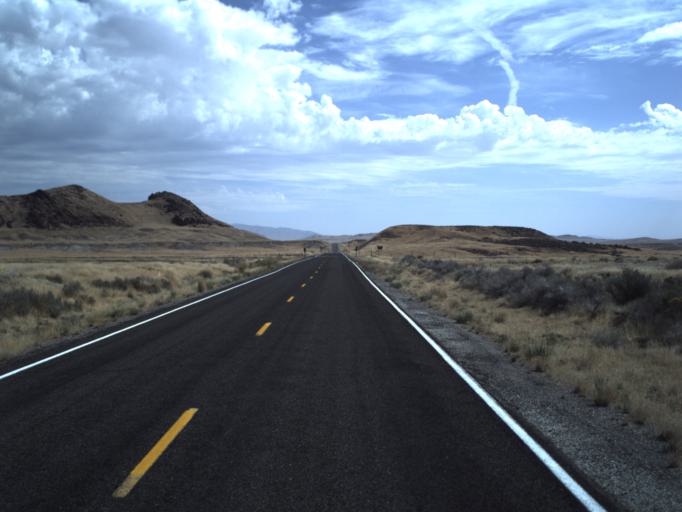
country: US
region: Nevada
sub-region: Elko County
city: West Wendover
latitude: 41.3727
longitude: -114.0236
